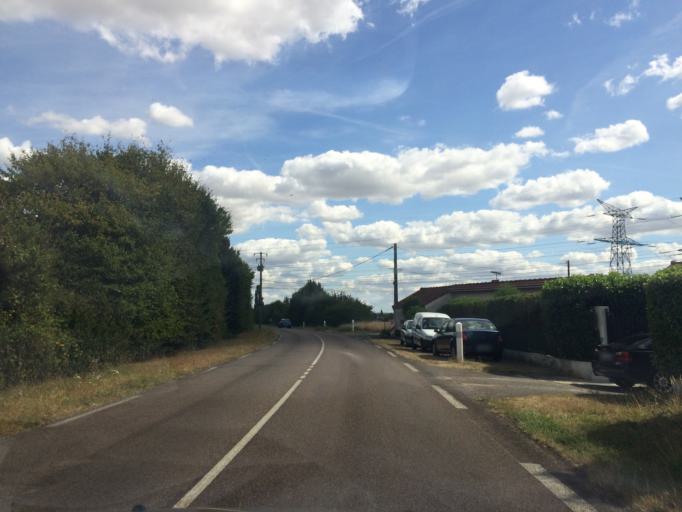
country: FR
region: Ile-de-France
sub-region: Departement de l'Essonne
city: Marolles-en-Hurepoix
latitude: 48.5529
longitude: 2.3124
